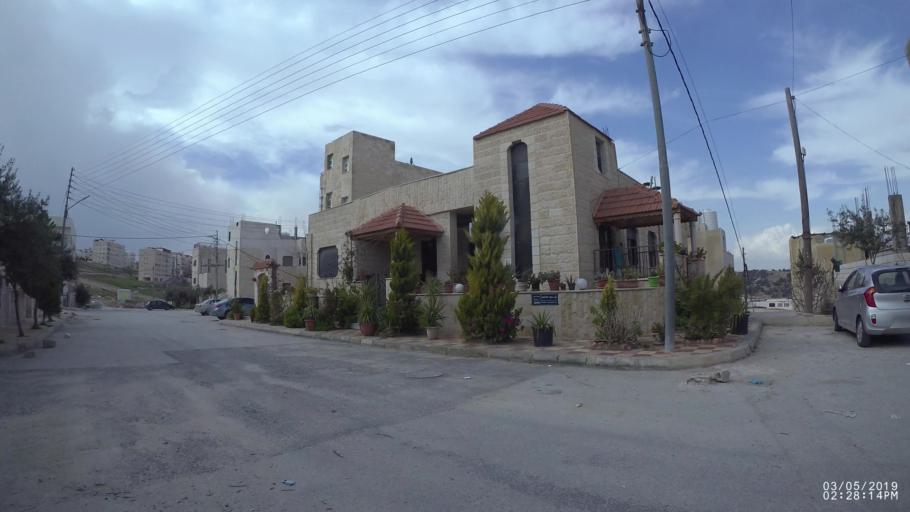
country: JO
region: Amman
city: Amman
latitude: 32.0139
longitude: 35.9439
